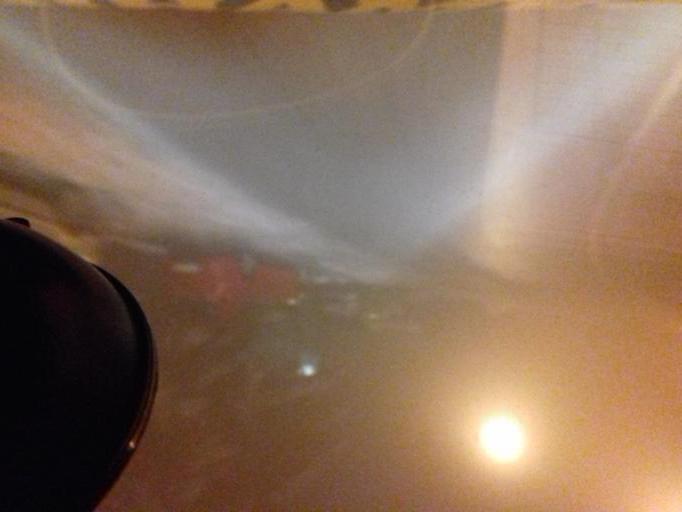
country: BA
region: Federation of Bosnia and Herzegovina
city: Kobilja Glava
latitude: 43.8657
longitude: 18.4158
